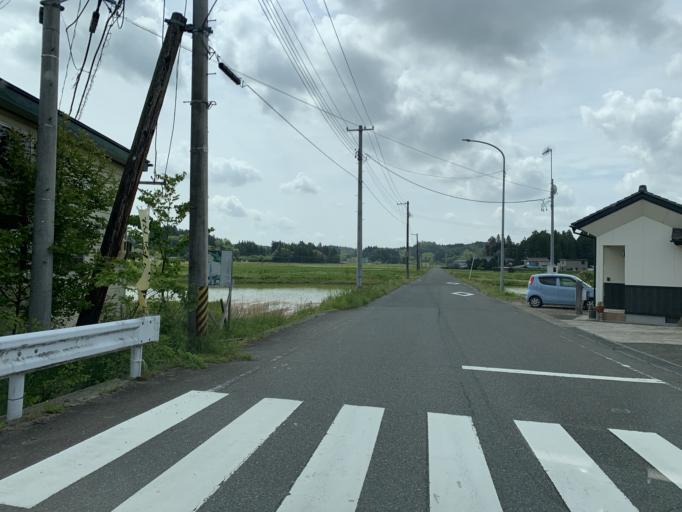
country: JP
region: Iwate
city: Ichinoseki
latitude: 38.8488
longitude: 141.0175
